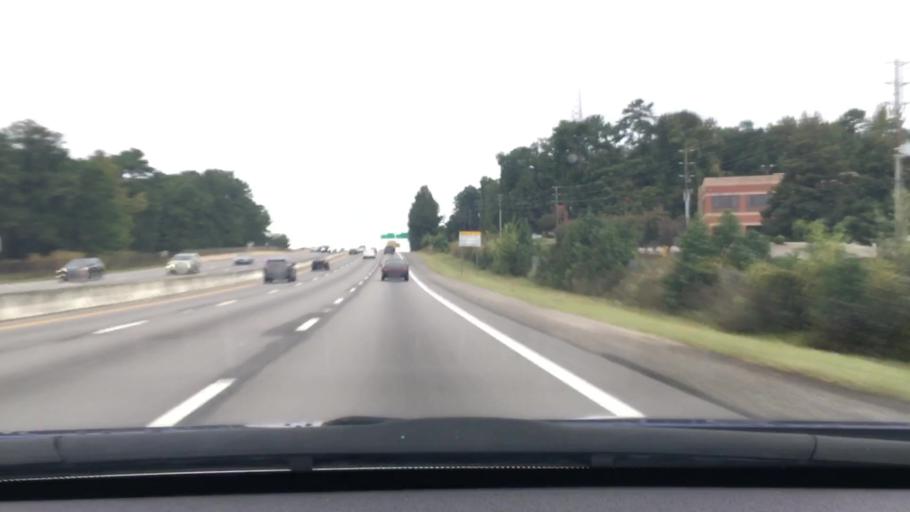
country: US
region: South Carolina
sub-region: Lexington County
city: Seven Oaks
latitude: 34.0614
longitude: -81.1359
